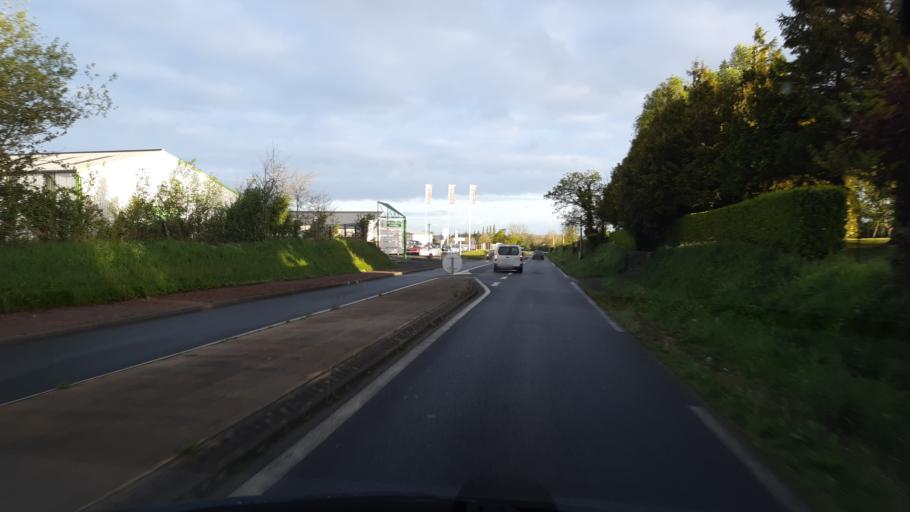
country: FR
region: Lower Normandy
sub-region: Departement de la Manche
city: Agneaux
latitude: 49.0522
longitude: -1.1299
